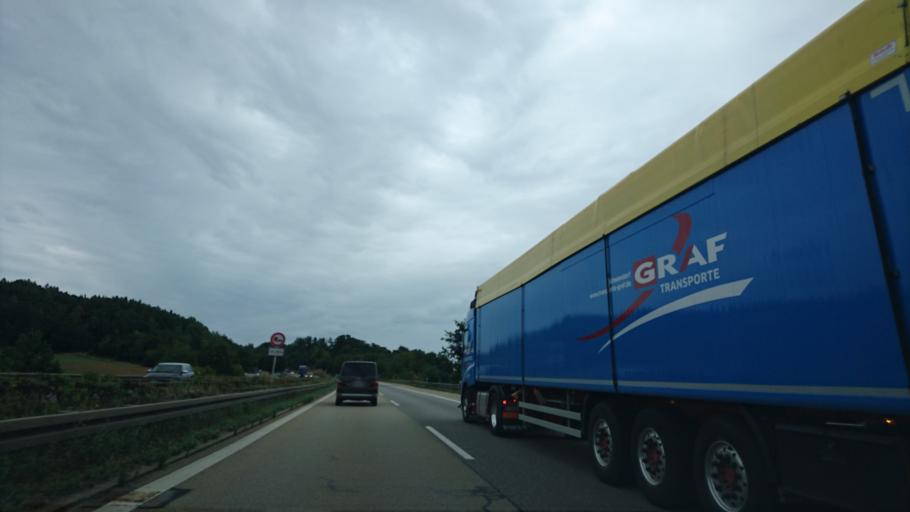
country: DE
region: Bavaria
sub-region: Upper Palatinate
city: Zeitlarn
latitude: 49.0733
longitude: 12.0972
